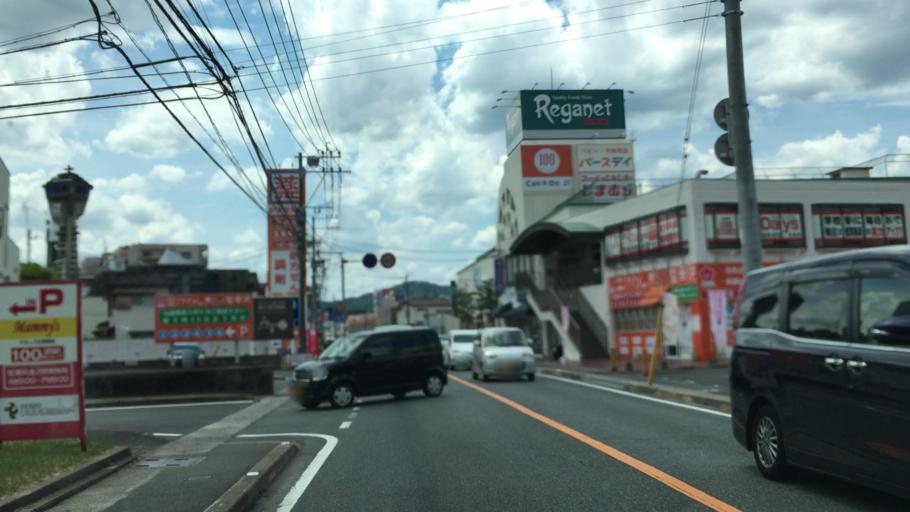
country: JP
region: Fukuoka
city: Dazaifu
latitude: 33.5106
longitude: 130.5249
